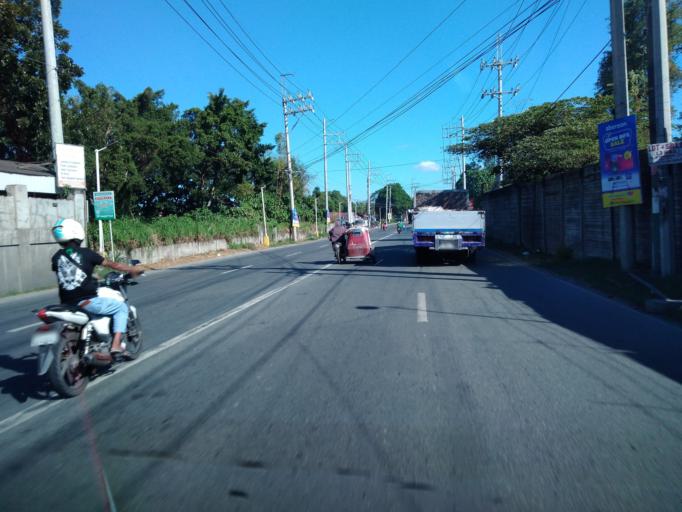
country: PH
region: Central Luzon
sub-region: Province of Bulacan
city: Santa Maria
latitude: 14.8150
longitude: 120.9488
